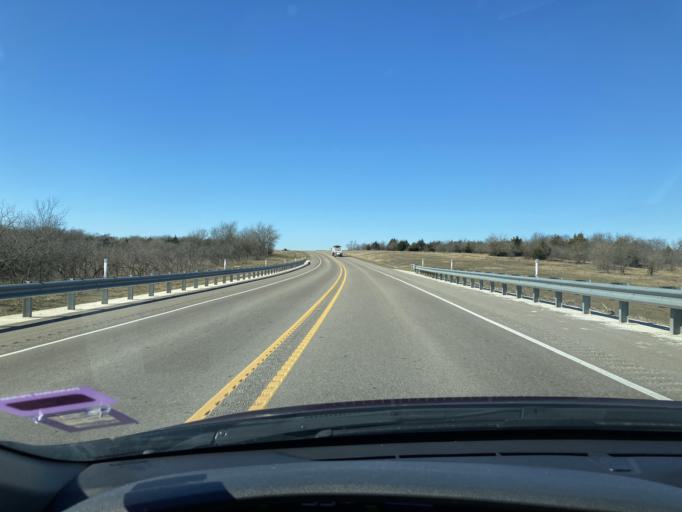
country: US
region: Texas
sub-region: Navarro County
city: Corsicana
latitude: 32.0478
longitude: -96.4754
